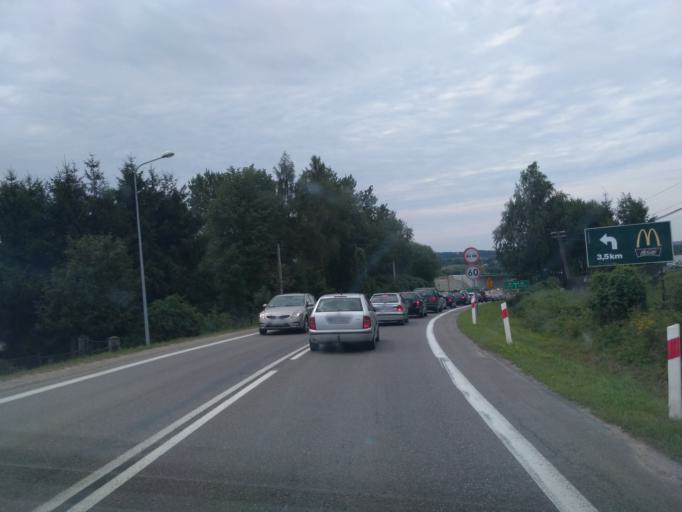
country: PL
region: Subcarpathian Voivodeship
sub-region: Powiat sanocki
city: Sanok
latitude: 49.5720
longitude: 22.1514
